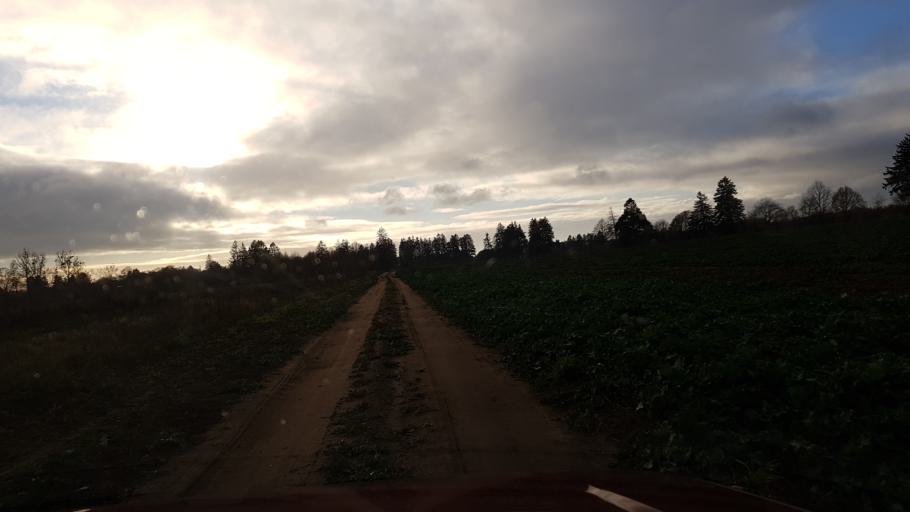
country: PL
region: West Pomeranian Voivodeship
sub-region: Powiat szczecinecki
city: Grzmiaca
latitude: 53.9859
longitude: 16.3996
